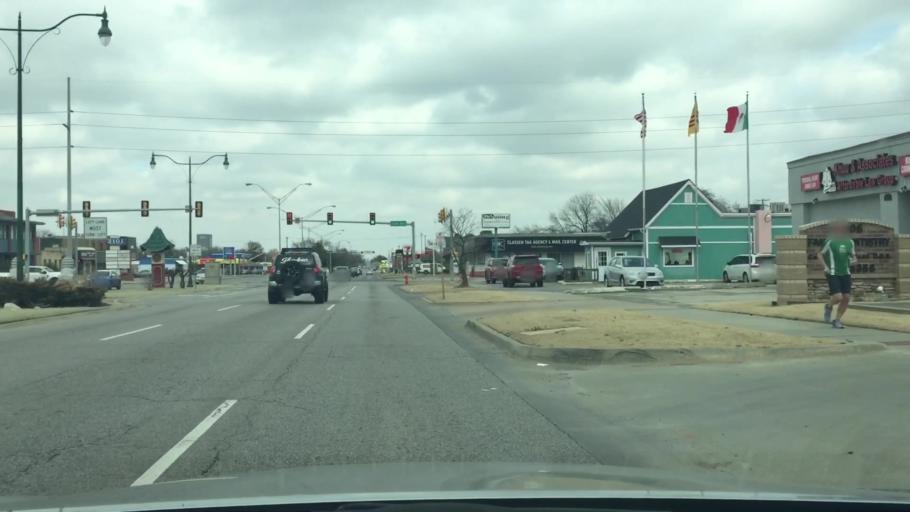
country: US
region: Oklahoma
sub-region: Oklahoma County
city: Oklahoma City
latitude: 35.4998
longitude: -97.5342
